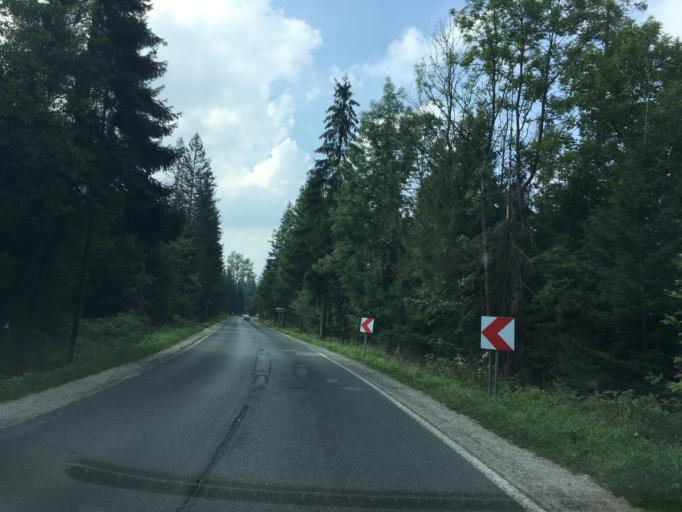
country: PL
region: Lesser Poland Voivodeship
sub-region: Powiat tatrzanski
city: Koscielisko
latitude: 49.2788
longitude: 19.8634
